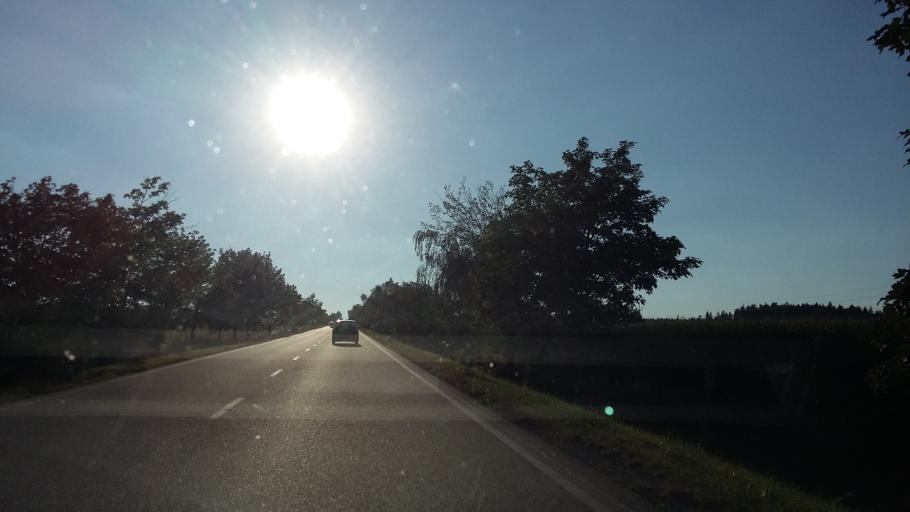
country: CZ
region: Vysocina
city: Merin
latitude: 49.4007
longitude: 15.8355
